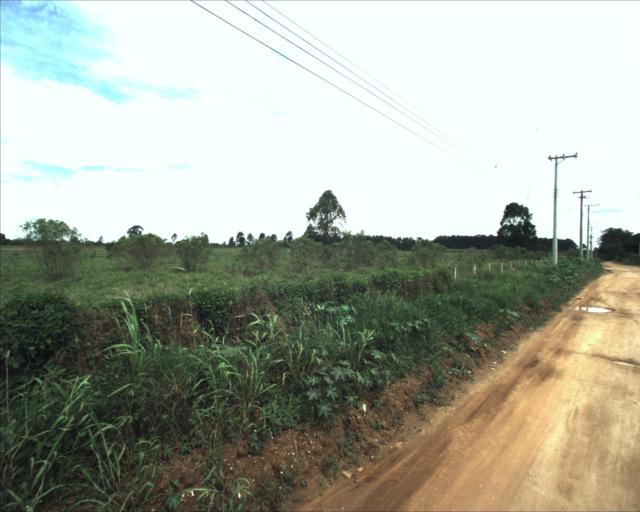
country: BR
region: Sao Paulo
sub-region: Aracoiaba Da Serra
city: Aracoiaba da Serra
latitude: -23.5599
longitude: -47.5562
